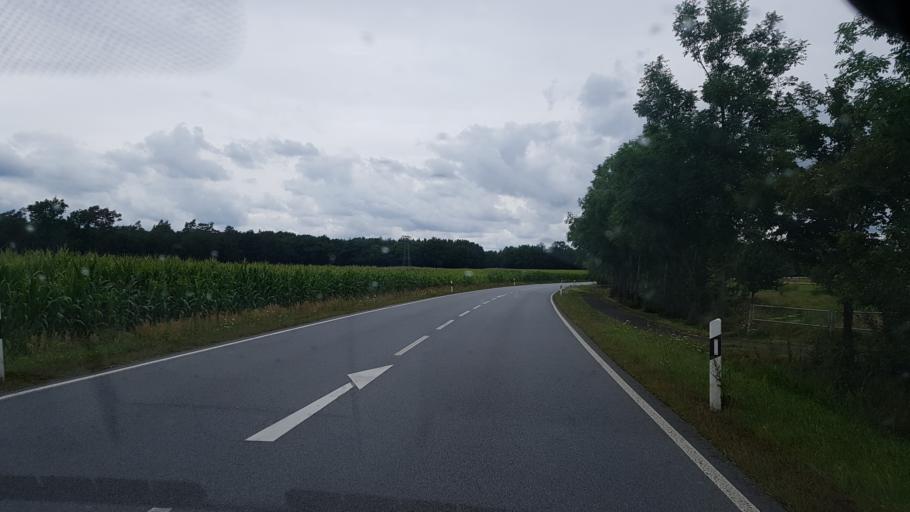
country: DE
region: Saxony
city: Niesky
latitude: 51.2624
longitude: 14.8085
